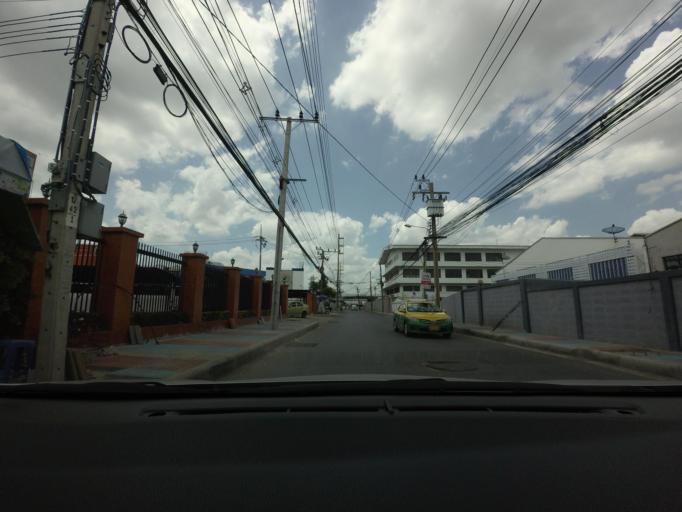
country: TH
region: Samut Prakan
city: Phra Samut Chedi
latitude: 13.6383
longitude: 100.5757
